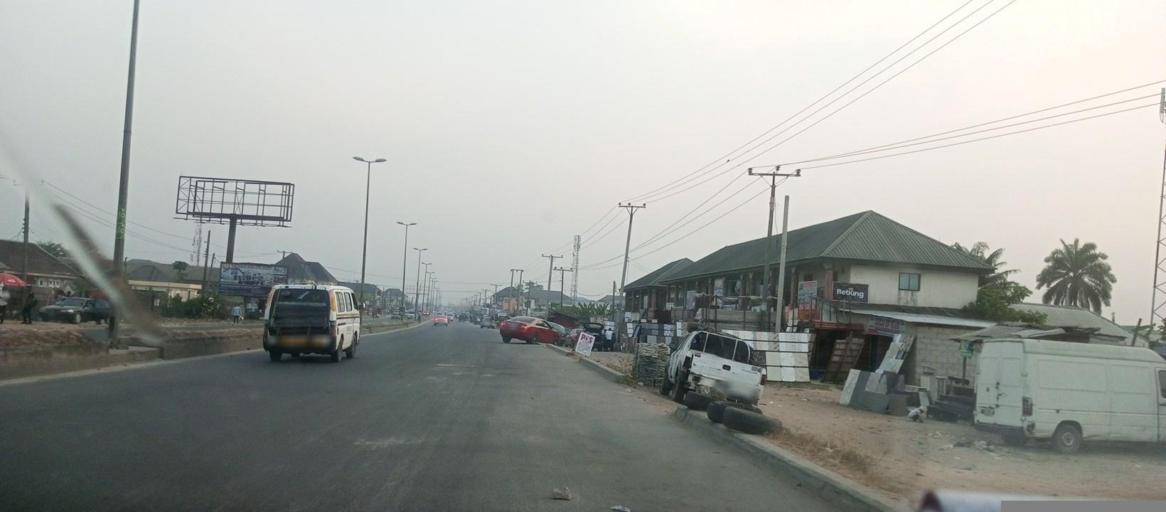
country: NG
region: Rivers
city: Emuoha
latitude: 4.9186
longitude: 6.9971
